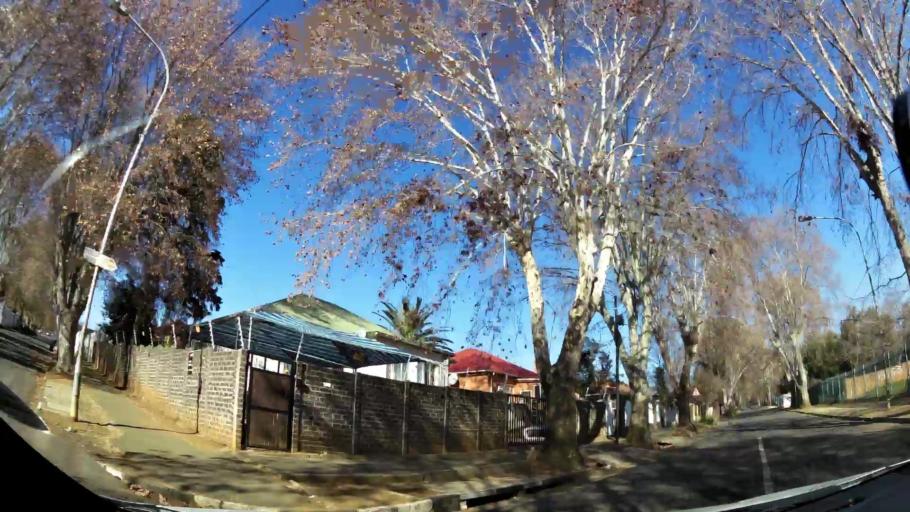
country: ZA
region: Gauteng
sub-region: City of Johannesburg Metropolitan Municipality
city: Johannesburg
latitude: -26.1891
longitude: 28.1038
